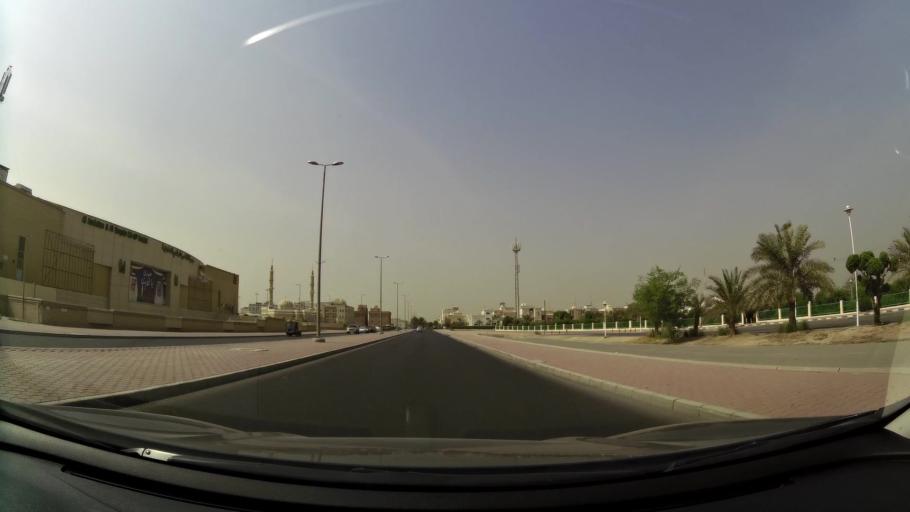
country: KW
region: Al Asimah
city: Ar Rabiyah
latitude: 29.3024
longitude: 47.9016
